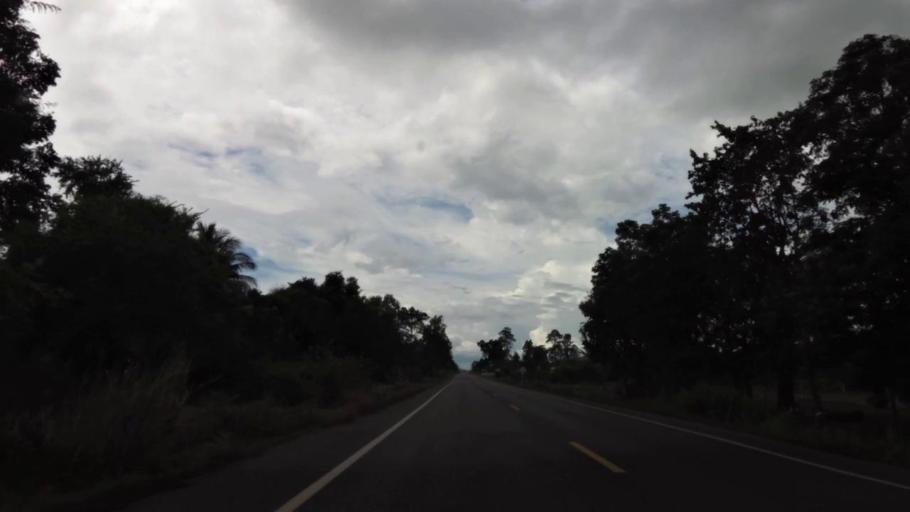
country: TH
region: Nakhon Sawan
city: Phai Sali
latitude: 15.5992
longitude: 100.6745
